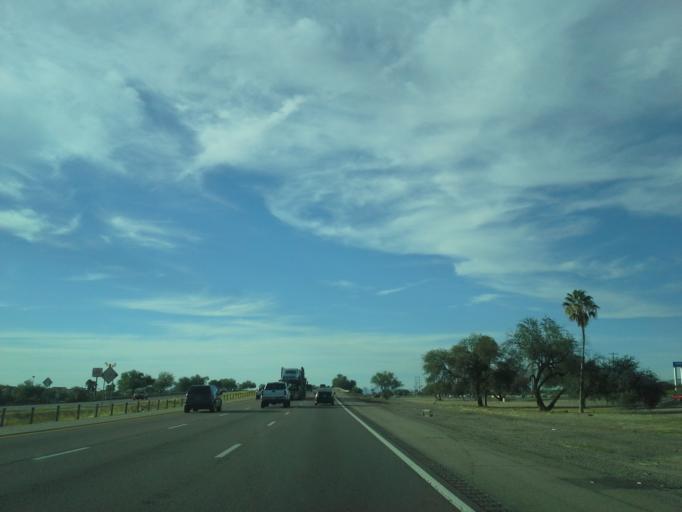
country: US
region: Arizona
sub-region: Pima County
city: Tortolita
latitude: 32.3560
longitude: -111.0866
